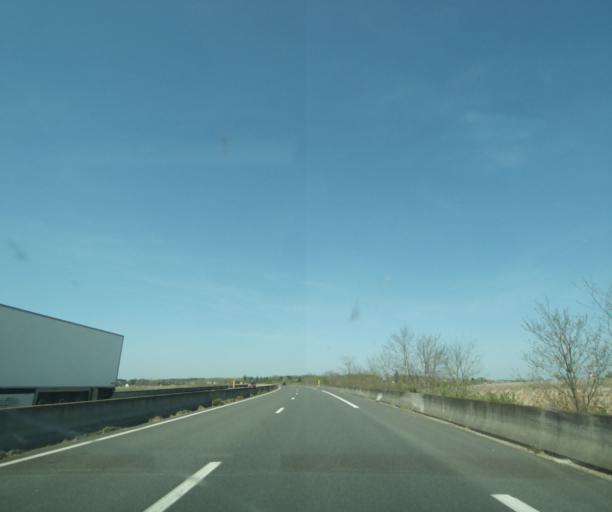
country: FR
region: Bourgogne
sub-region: Departement de la Nievre
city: Pouilly-sur-Loire
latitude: 47.2803
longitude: 2.9725
